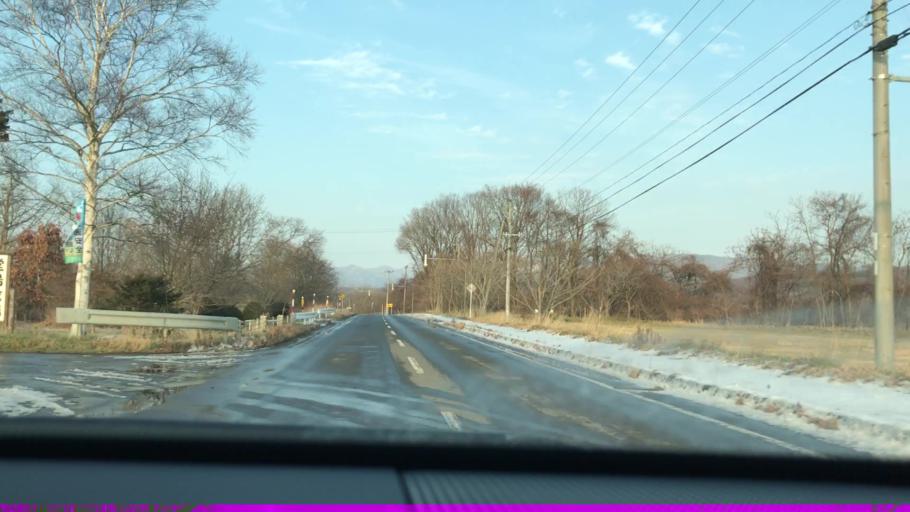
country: JP
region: Hokkaido
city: Shizunai-furukawacho
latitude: 42.4116
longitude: 142.3960
